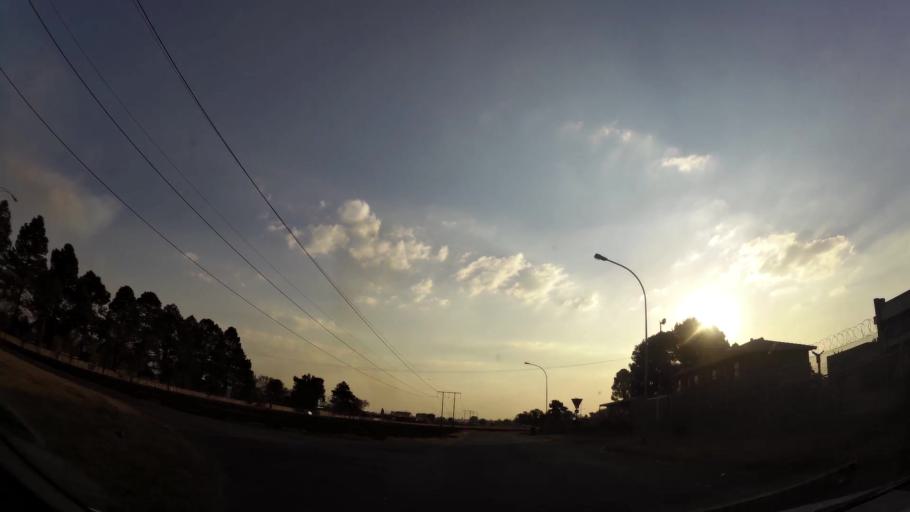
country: ZA
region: Gauteng
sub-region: Ekurhuleni Metropolitan Municipality
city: Springs
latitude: -26.2685
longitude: 28.4167
